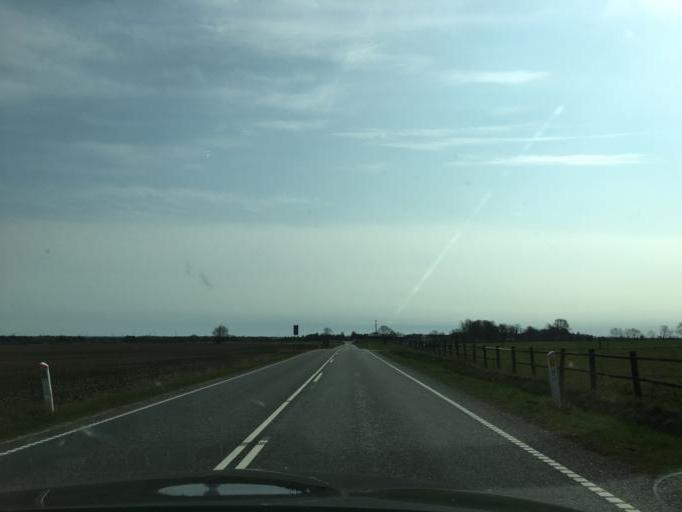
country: DK
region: South Denmark
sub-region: Vejen Kommune
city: Vejen
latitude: 55.4916
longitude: 9.0907
